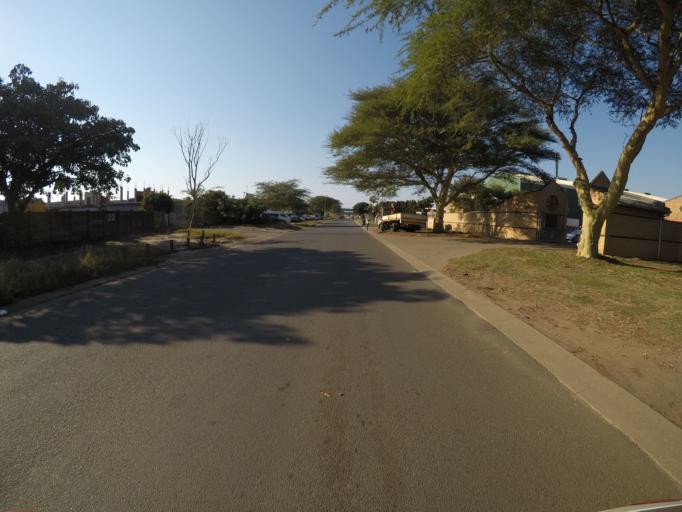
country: ZA
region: KwaZulu-Natal
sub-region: uThungulu District Municipality
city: Richards Bay
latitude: -28.7505
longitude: 32.0218
